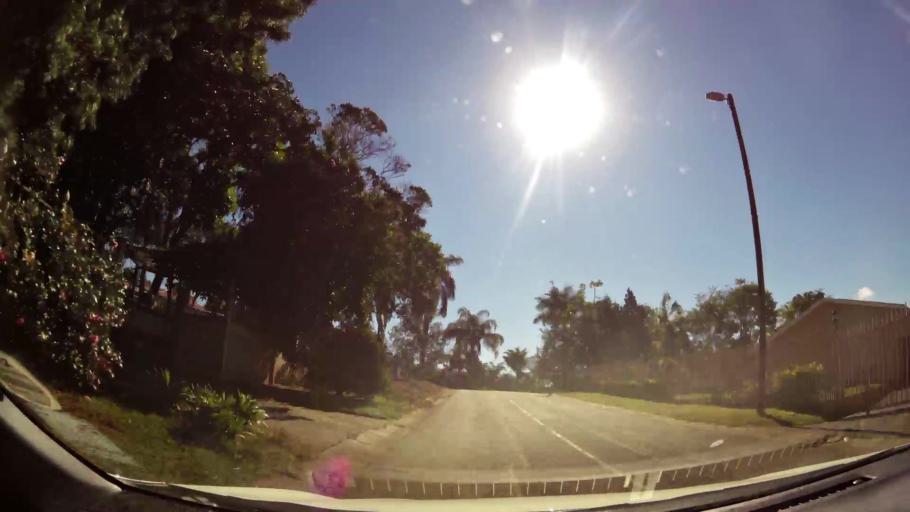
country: ZA
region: Limpopo
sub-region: Mopani District Municipality
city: Tzaneen
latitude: -23.8266
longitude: 30.1453
